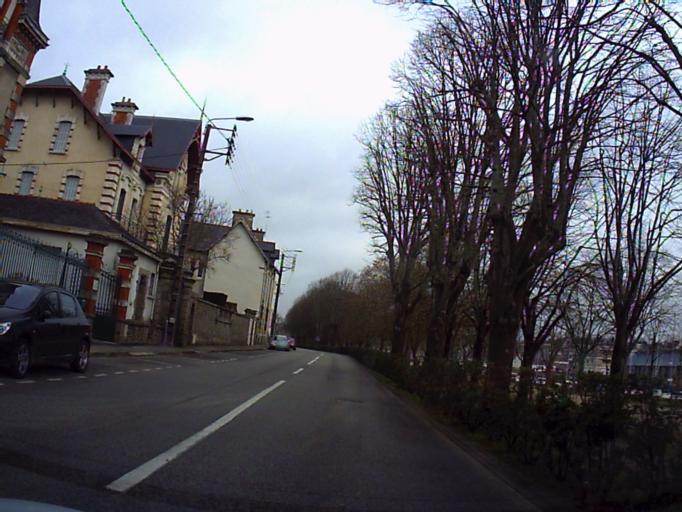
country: FR
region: Brittany
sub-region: Departement du Morbihan
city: Vannes
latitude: 47.6478
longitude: -2.7585
